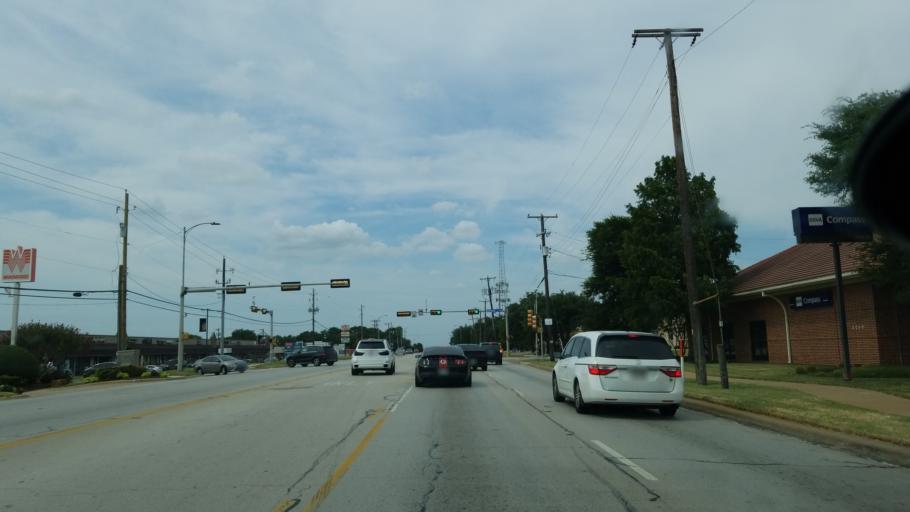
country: US
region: Texas
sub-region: Tarrant County
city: Arlington
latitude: 32.7698
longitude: -97.0970
